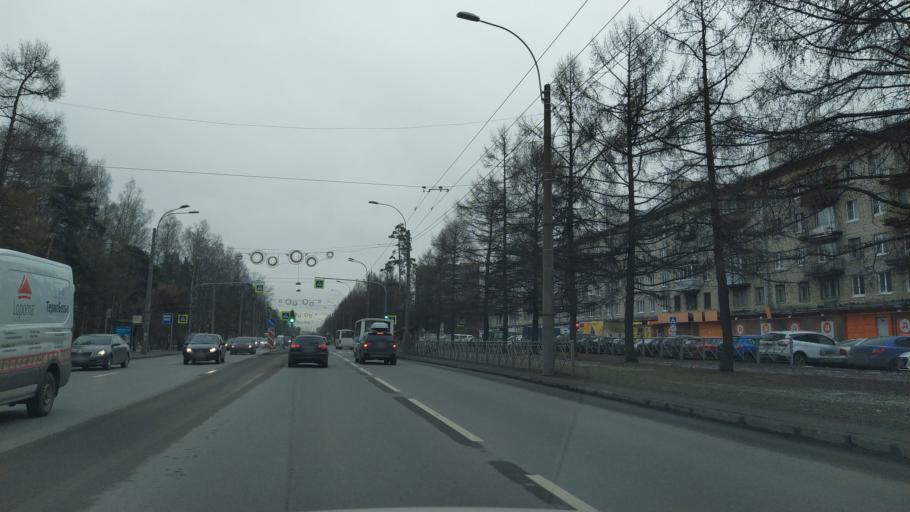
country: RU
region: St.-Petersburg
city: Sosnovka
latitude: 60.0168
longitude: 30.3373
